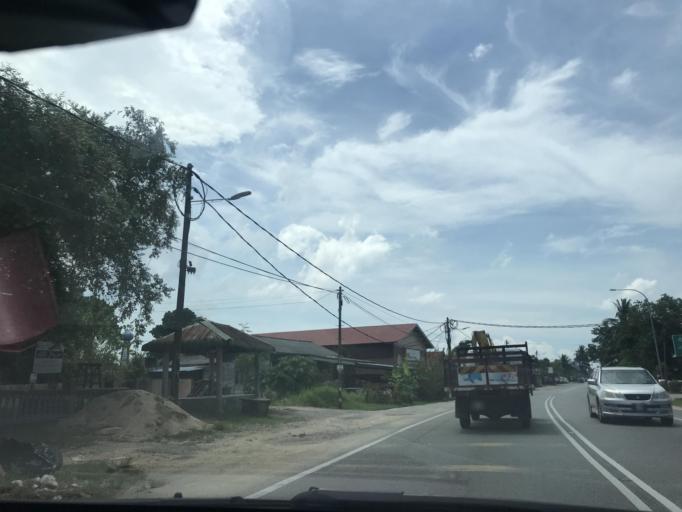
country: MY
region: Kelantan
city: Kota Bharu
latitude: 6.0993
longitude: 102.2303
